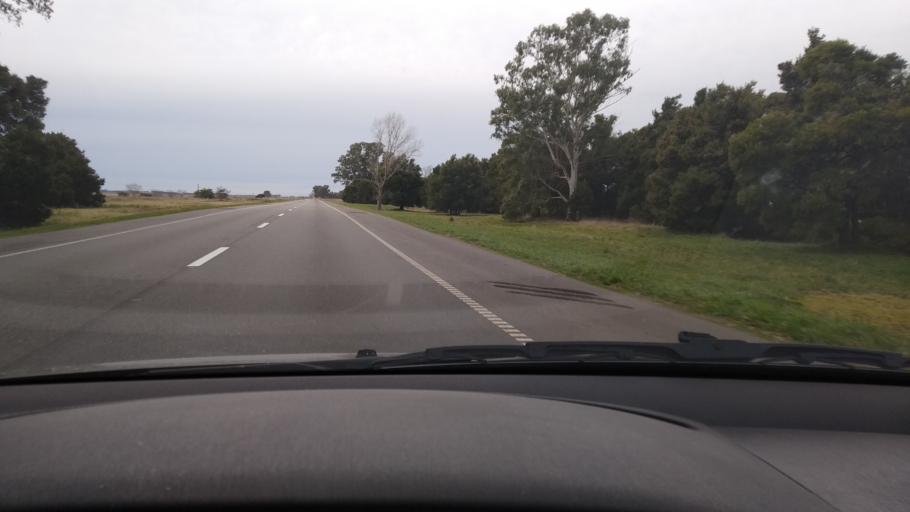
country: AR
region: Buenos Aires
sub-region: Partido de Las Flores
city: Las Flores
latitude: -36.3794
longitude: -59.4815
